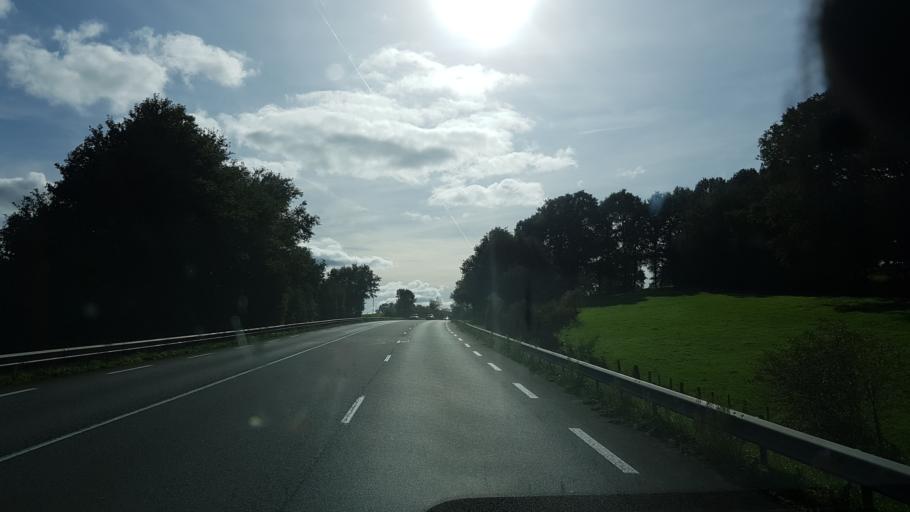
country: FR
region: Poitou-Charentes
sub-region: Departement de la Charente
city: Confolens
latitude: 46.0103
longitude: 0.6428
